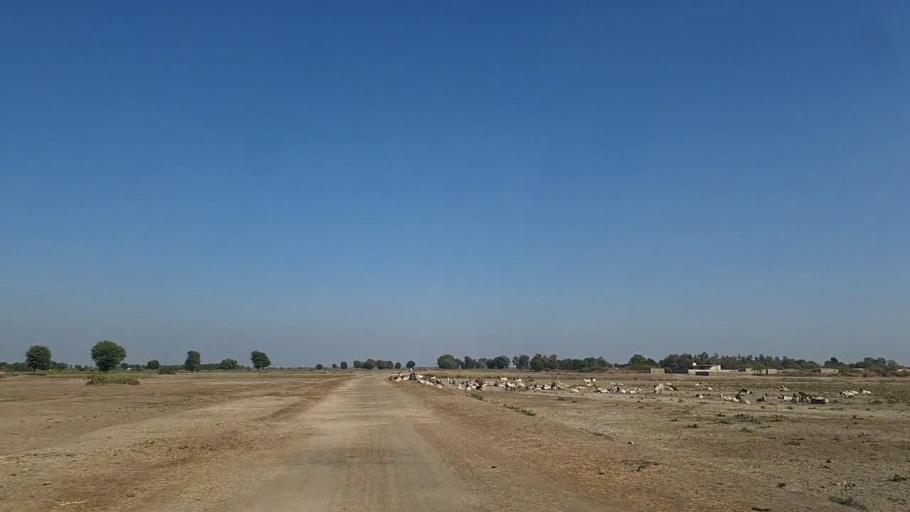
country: PK
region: Sindh
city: Samaro
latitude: 25.3518
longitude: 69.4298
